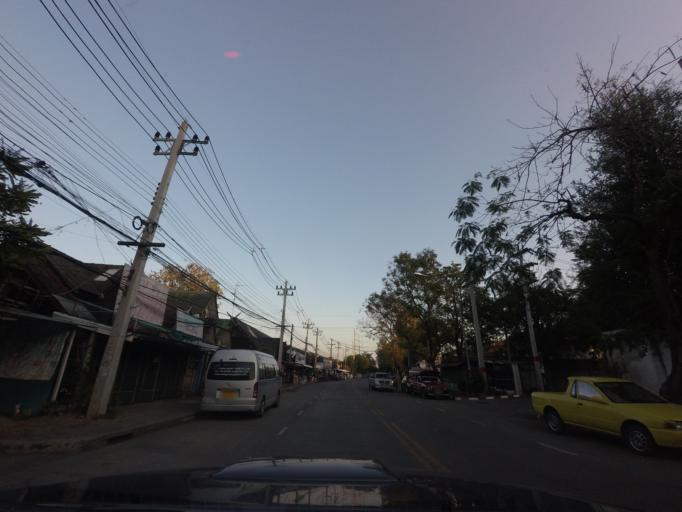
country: TH
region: Chiang Mai
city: Chiang Mai
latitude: 18.7749
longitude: 98.9789
